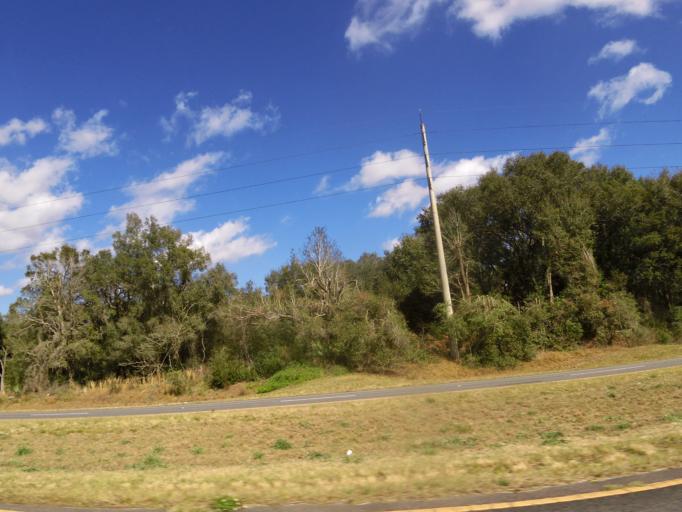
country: US
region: Florida
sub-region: Volusia County
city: North DeLand
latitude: 29.0799
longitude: -81.3160
